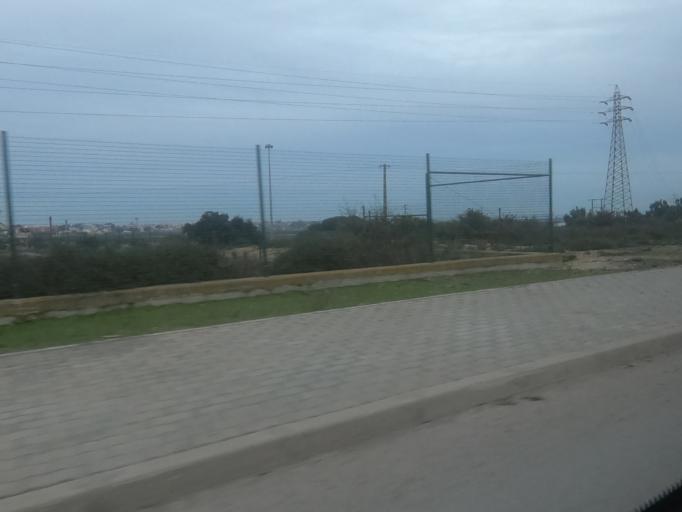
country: PT
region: Setubal
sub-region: Setubal
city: Setubal
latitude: 38.5084
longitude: -8.8328
